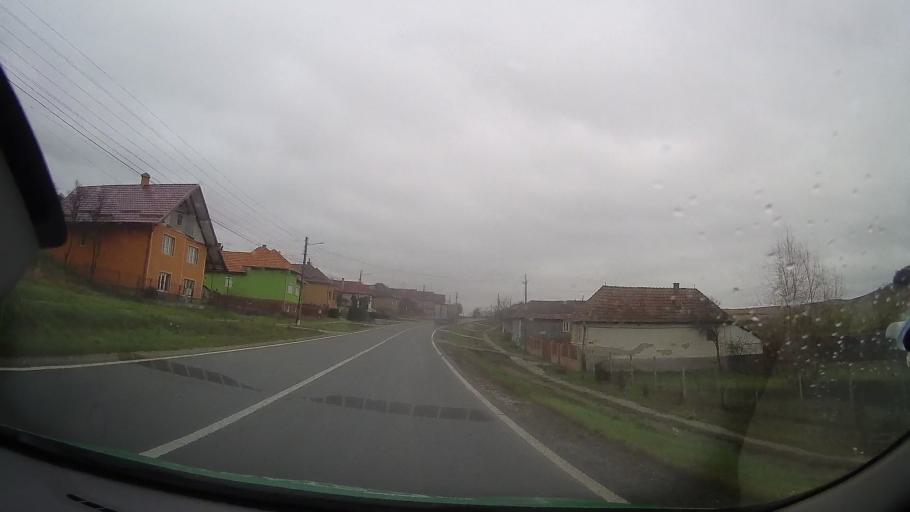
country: RO
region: Mures
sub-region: Comuna Lunca
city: Lunca
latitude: 46.8560
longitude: 24.5687
